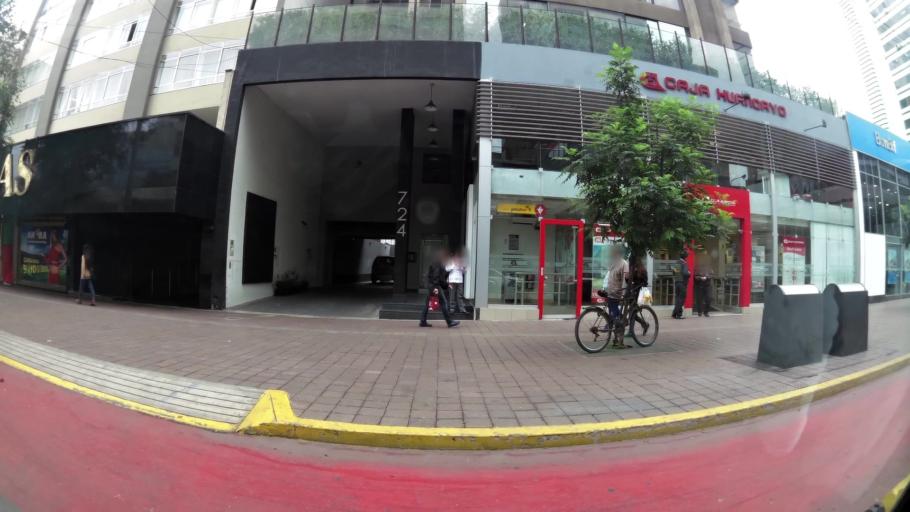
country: PE
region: Lima
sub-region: Lima
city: San Isidro
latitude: -12.1249
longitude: -77.0295
